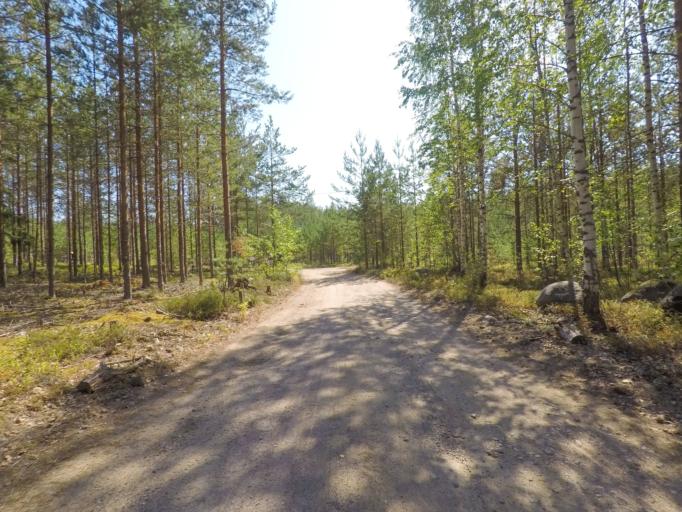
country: FI
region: Southern Savonia
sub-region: Mikkeli
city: Puumala
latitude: 61.4273
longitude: 28.0080
